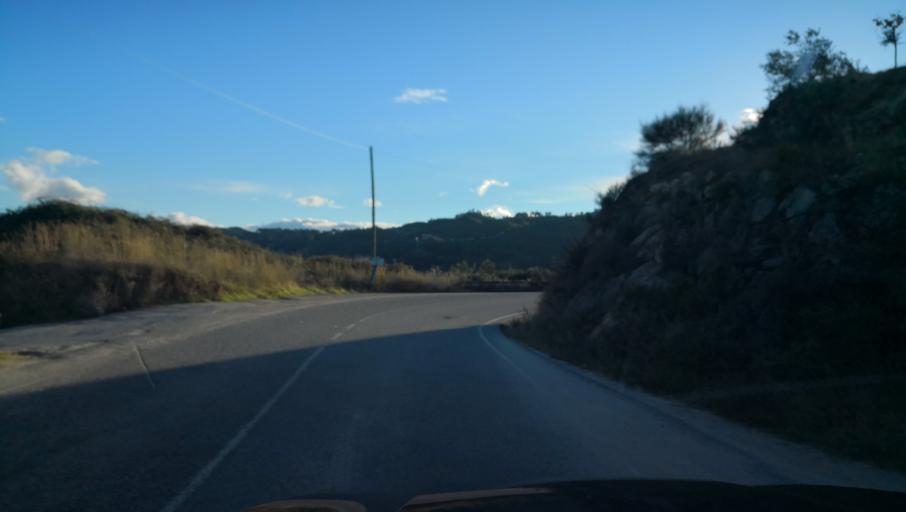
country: PT
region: Vila Real
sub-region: Vila Real
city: Vila Real
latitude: 41.2738
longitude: -7.7690
